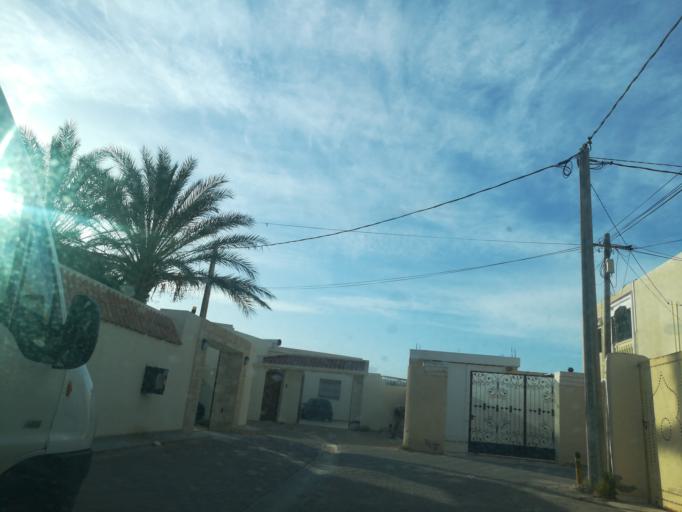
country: TN
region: Safaqis
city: Al Qarmadah
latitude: 34.8090
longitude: 10.7553
